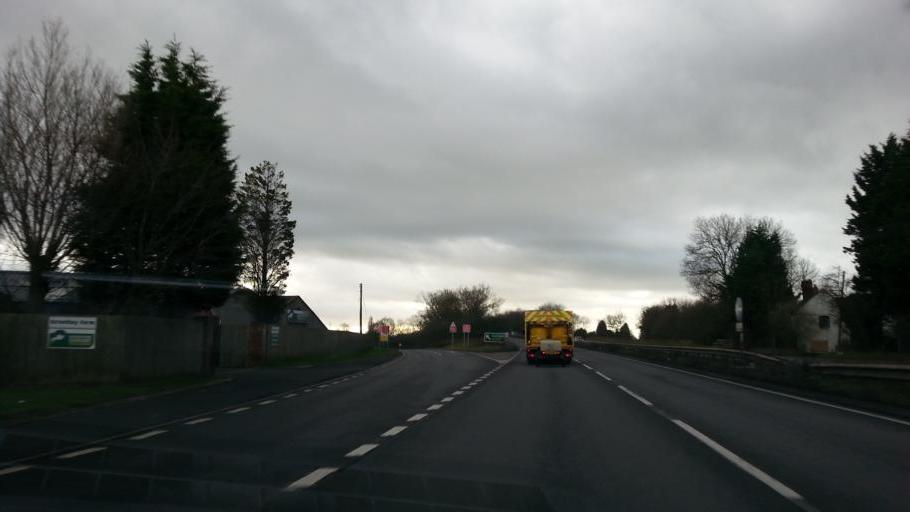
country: GB
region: England
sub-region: Staffordshire
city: Whittington
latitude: 52.6952
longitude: -1.7858
